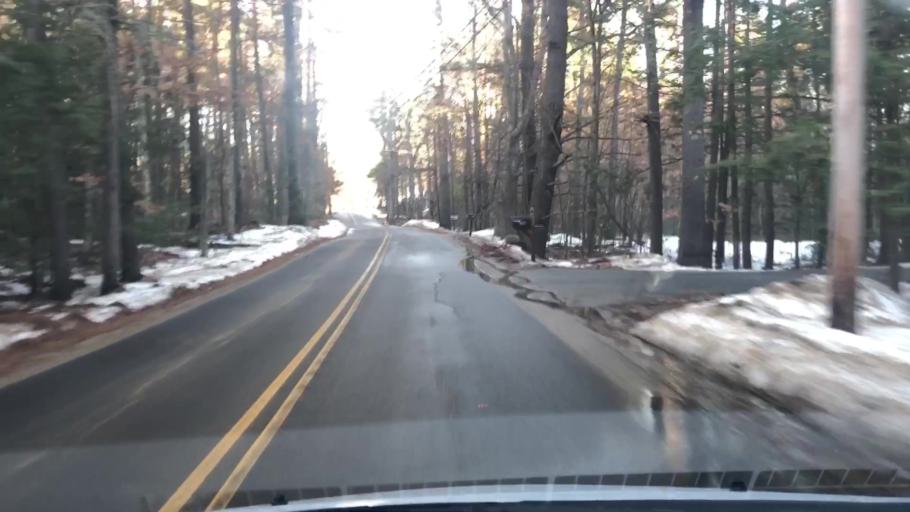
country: US
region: New Hampshire
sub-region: Hillsborough County
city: Milford
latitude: 42.8033
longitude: -71.6465
